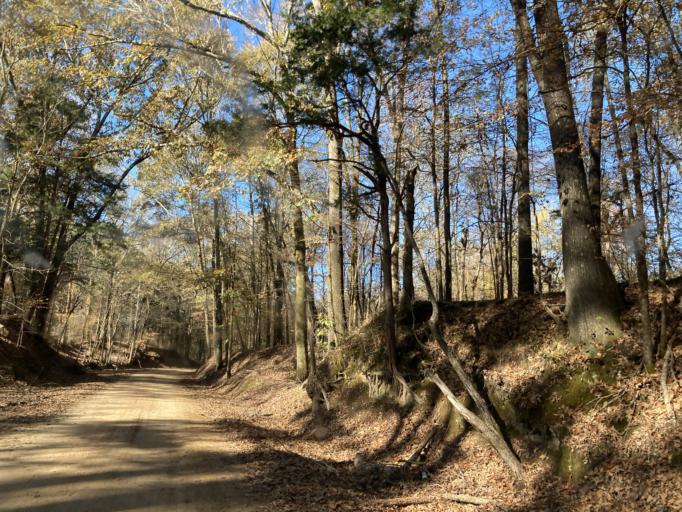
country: US
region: Mississippi
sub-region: Hinds County
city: Lynchburg
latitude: 32.6224
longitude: -90.5248
